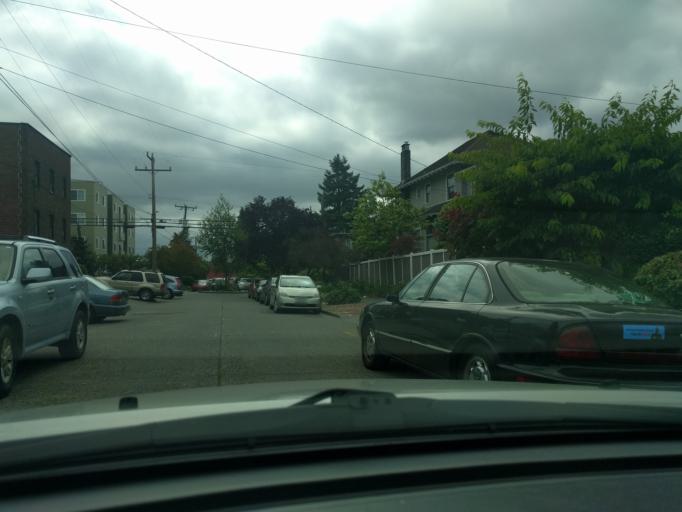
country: US
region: Washington
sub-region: King County
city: Seattle
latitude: 47.6607
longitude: -122.3494
